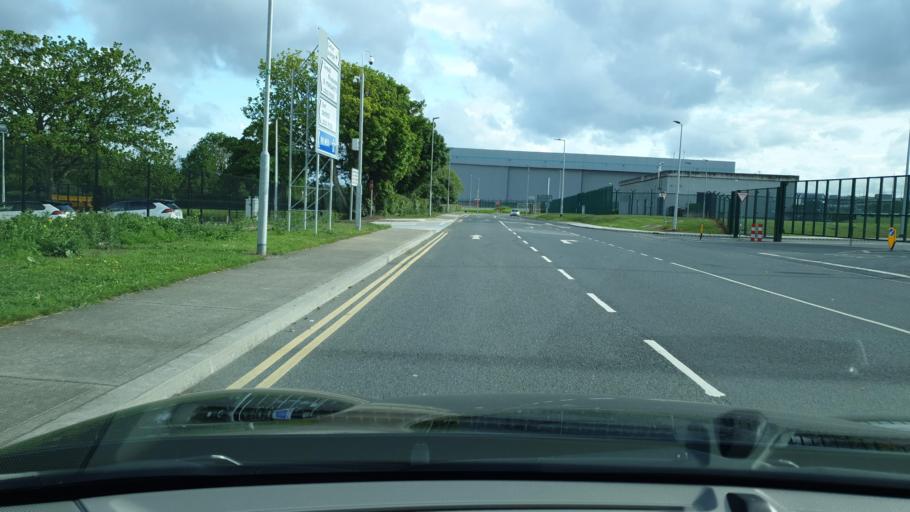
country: IE
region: Leinster
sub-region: Fingal County
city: Swords
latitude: 53.4335
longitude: -6.2318
